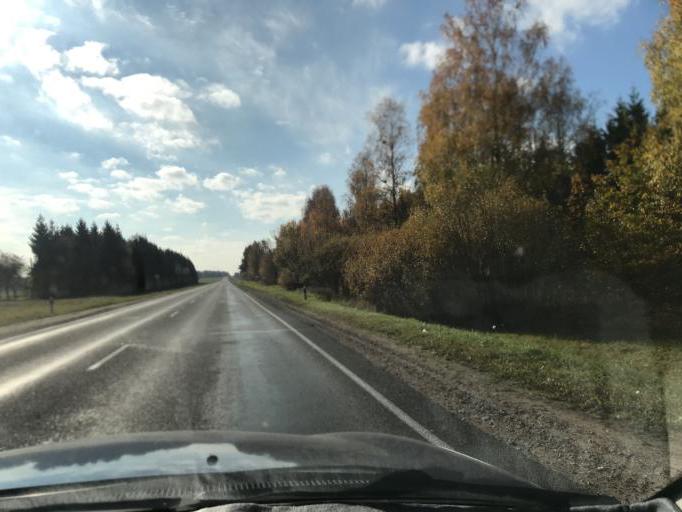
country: BY
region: Grodnenskaya
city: Voranava
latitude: 54.2048
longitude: 25.3493
